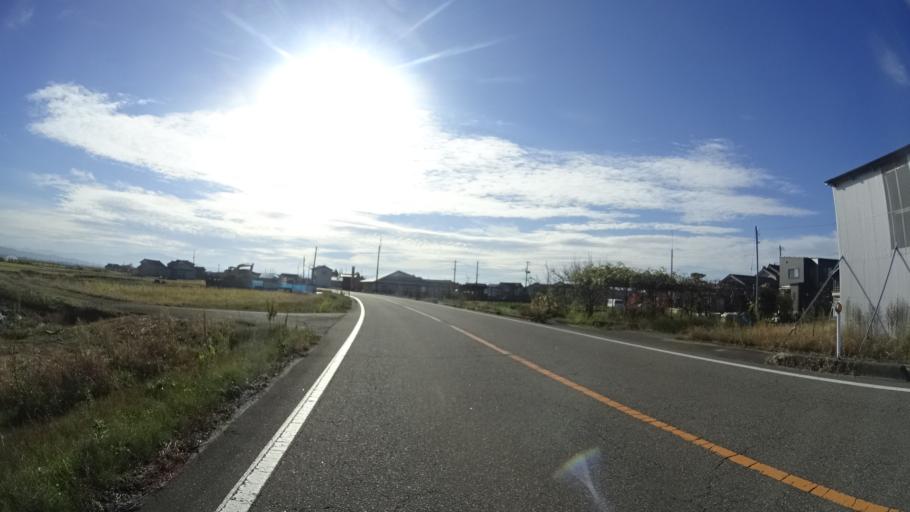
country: JP
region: Niigata
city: Mitsuke
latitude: 37.5775
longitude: 138.8353
